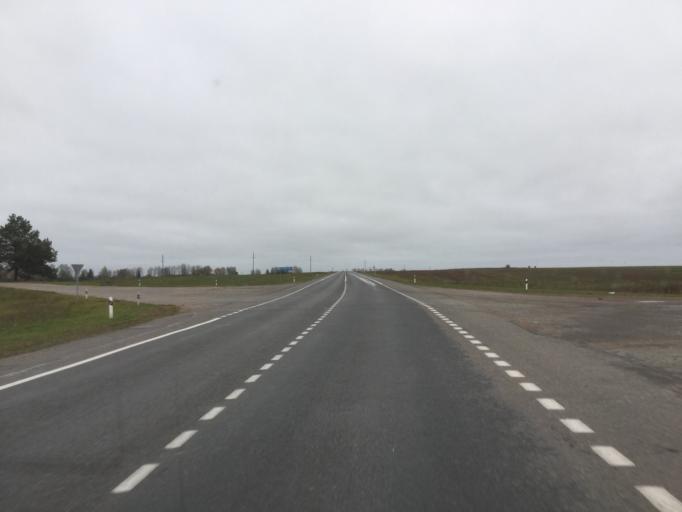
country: BY
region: Vitebsk
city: Chashniki
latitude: 55.0087
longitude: 29.1571
